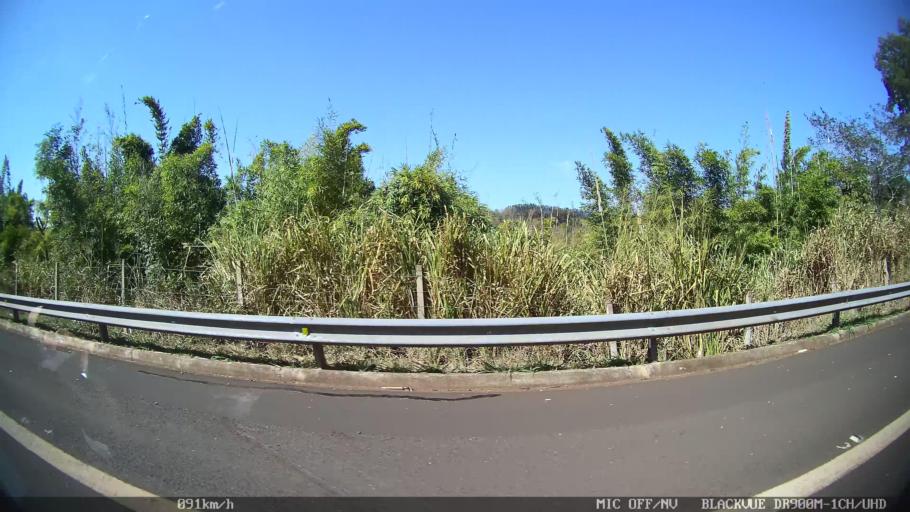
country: BR
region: Sao Paulo
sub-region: Batatais
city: Batatais
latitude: -20.7329
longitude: -47.5260
